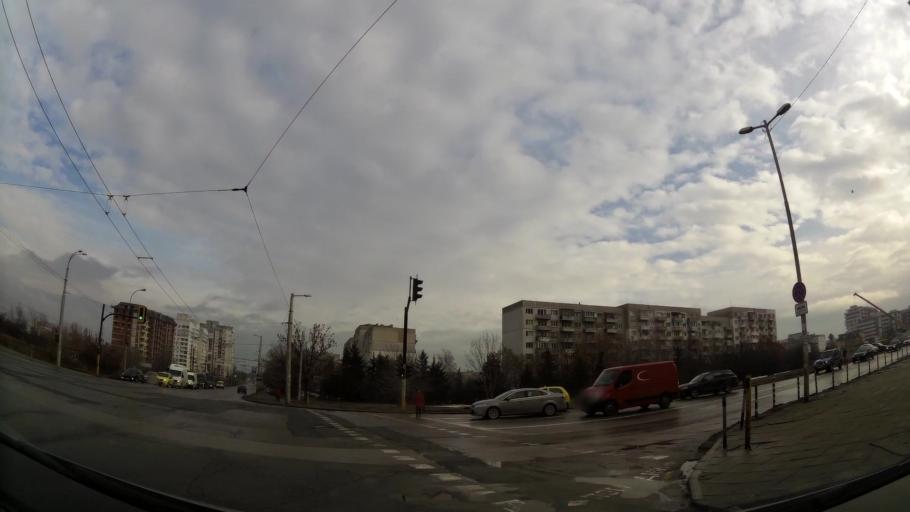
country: BG
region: Sofiya
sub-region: Obshtina Bozhurishte
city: Bozhurishte
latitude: 42.7253
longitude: 23.2443
